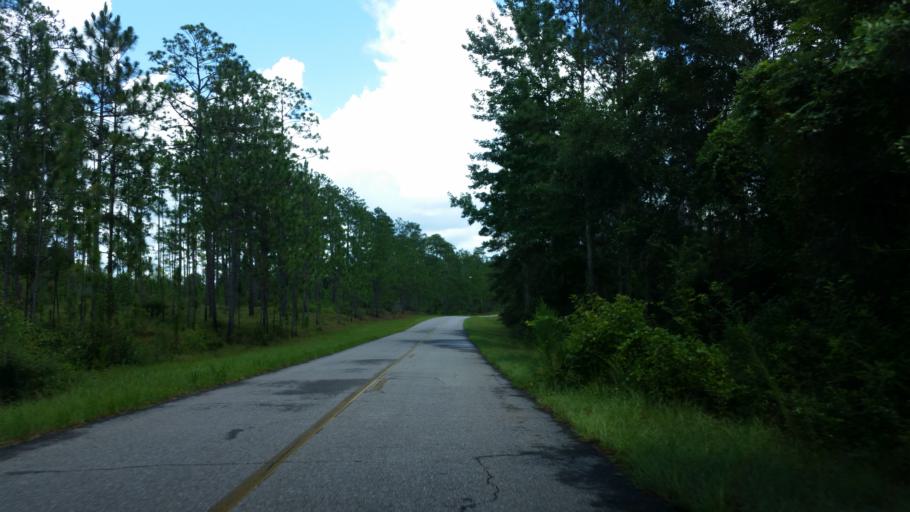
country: US
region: Florida
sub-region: Santa Rosa County
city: Point Baker
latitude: 30.7427
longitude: -86.8286
